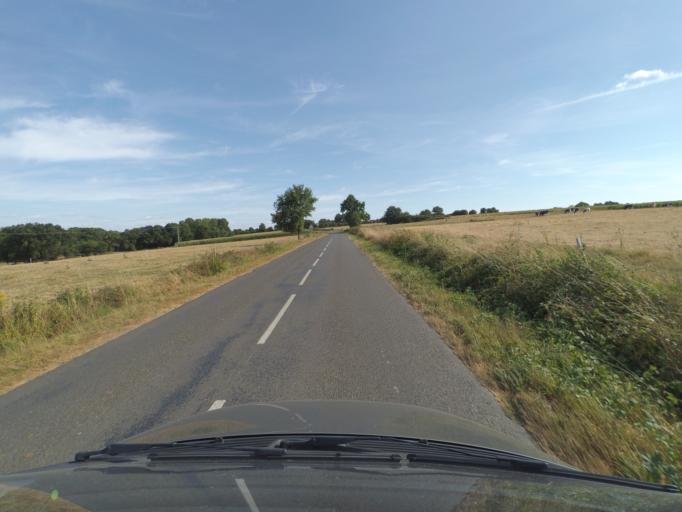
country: FR
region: Pays de la Loire
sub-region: Departement de la Loire-Atlantique
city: Montbert
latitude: 47.0488
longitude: -1.4821
